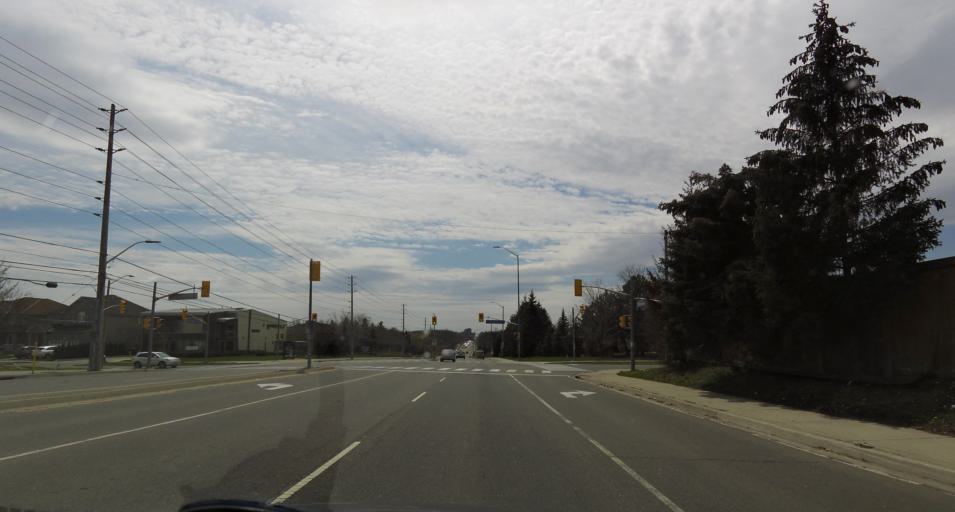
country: CA
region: Ontario
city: Mississauga
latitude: 43.5954
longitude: -79.7145
